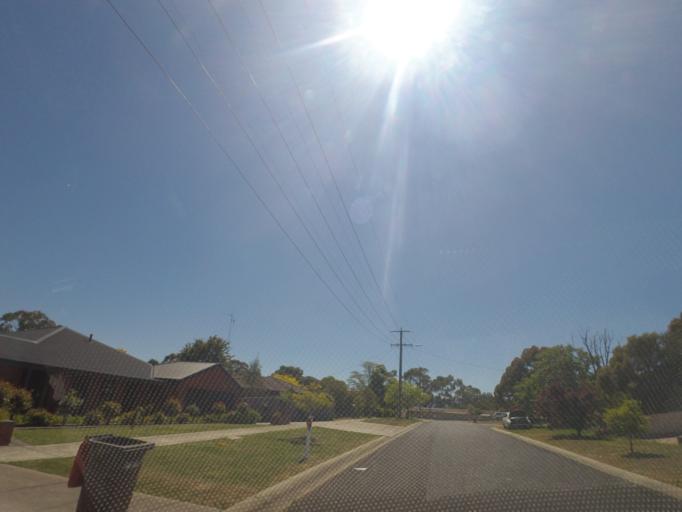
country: AU
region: Victoria
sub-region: Whittlesea
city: Whittlesea
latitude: -37.2079
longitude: 145.0615
